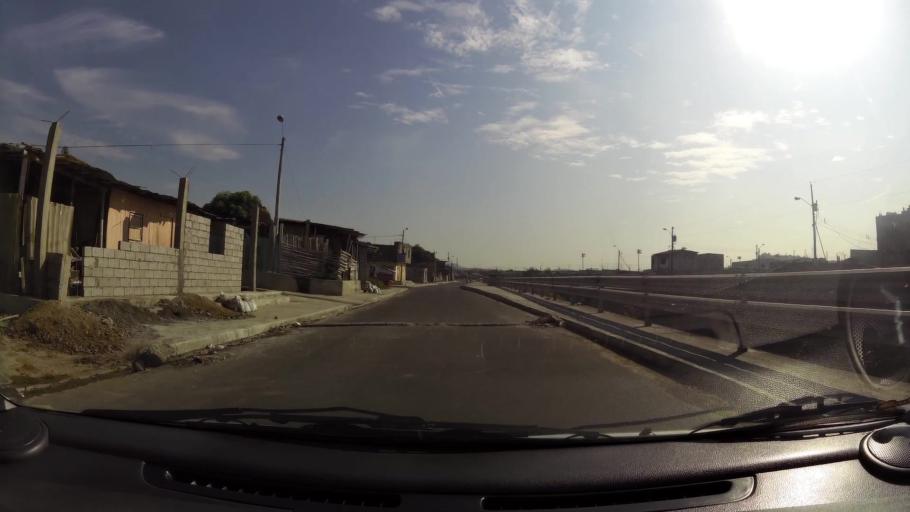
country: EC
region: Guayas
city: Eloy Alfaro
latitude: -2.0836
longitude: -79.9241
